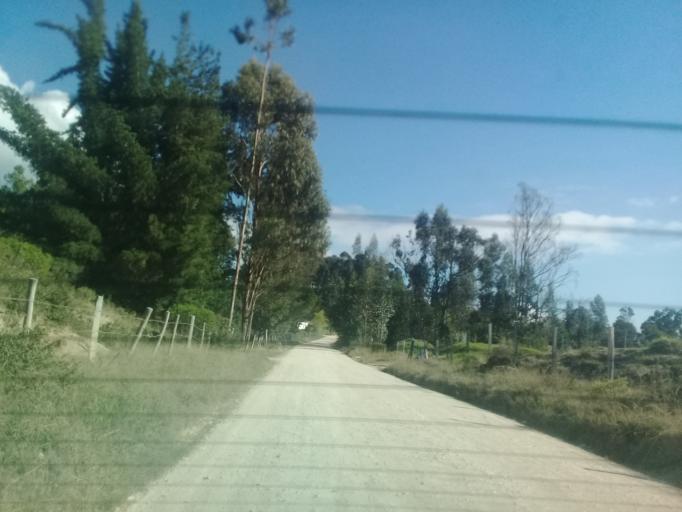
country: CO
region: Cundinamarca
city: Tocancipa
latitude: 4.9253
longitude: -73.8837
